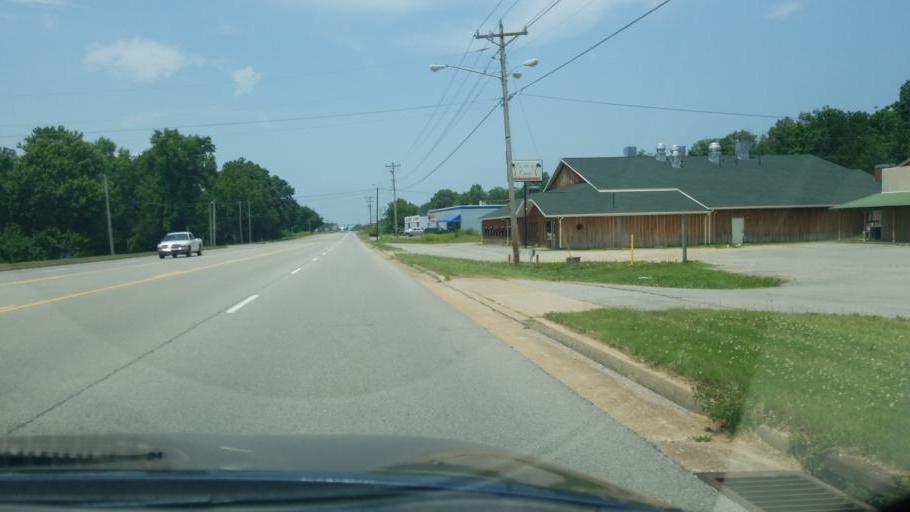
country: US
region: Tennessee
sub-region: Humphreys County
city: New Johnsonville
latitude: 36.0322
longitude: -87.9453
